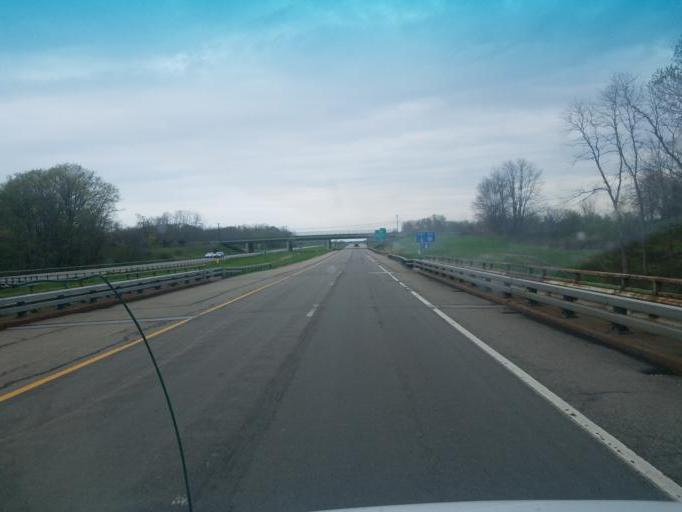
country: US
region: New York
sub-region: Chautauqua County
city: Westfield
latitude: 42.3331
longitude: -79.5920
